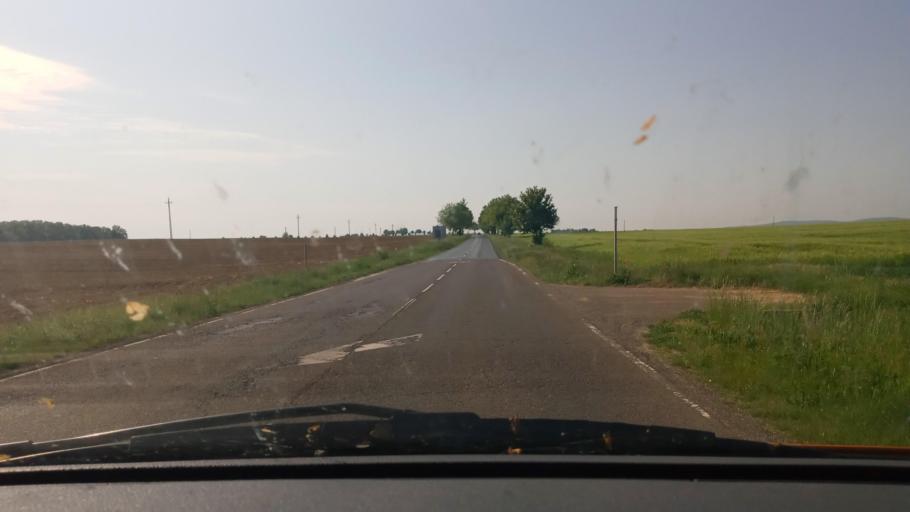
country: HU
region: Baranya
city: Kozarmisleny
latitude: 46.0156
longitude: 18.3044
